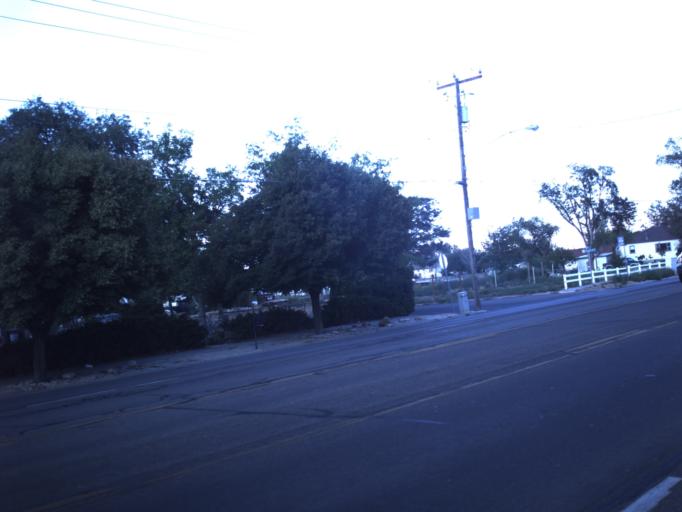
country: US
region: Utah
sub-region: Tooele County
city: Grantsville
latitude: 40.5997
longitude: -112.4537
